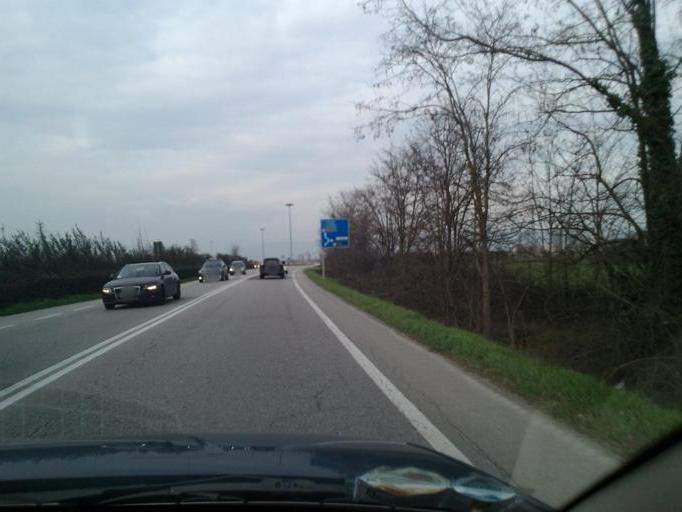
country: IT
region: Veneto
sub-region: Provincia di Verona
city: Sona
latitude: 45.4358
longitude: 10.8493
